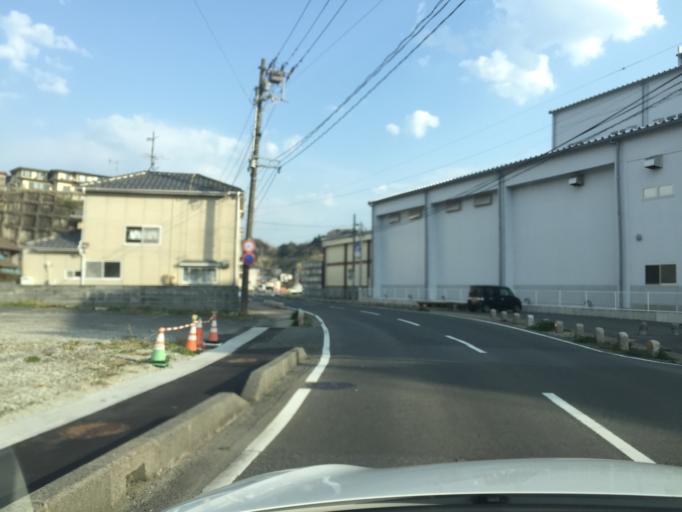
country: JP
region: Fukushima
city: Iwaki
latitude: 36.9433
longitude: 140.9148
